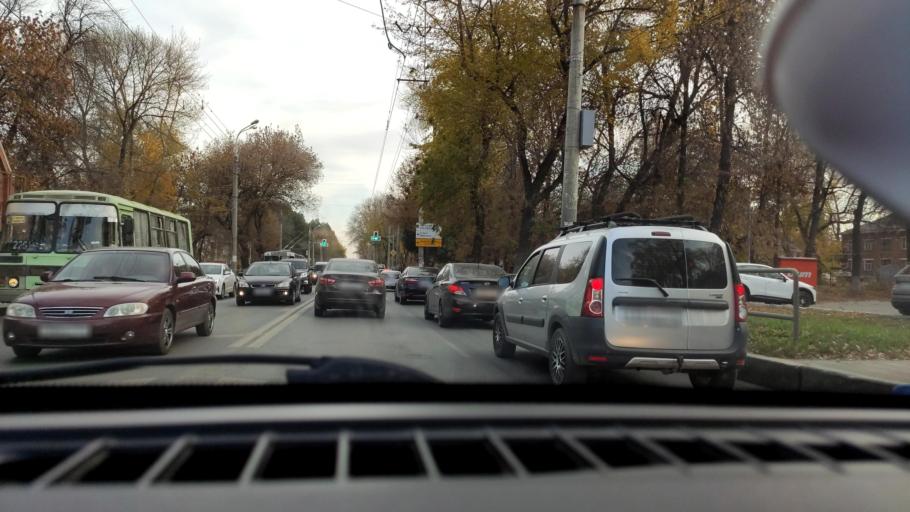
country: RU
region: Samara
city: Samara
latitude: 53.2370
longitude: 50.2405
